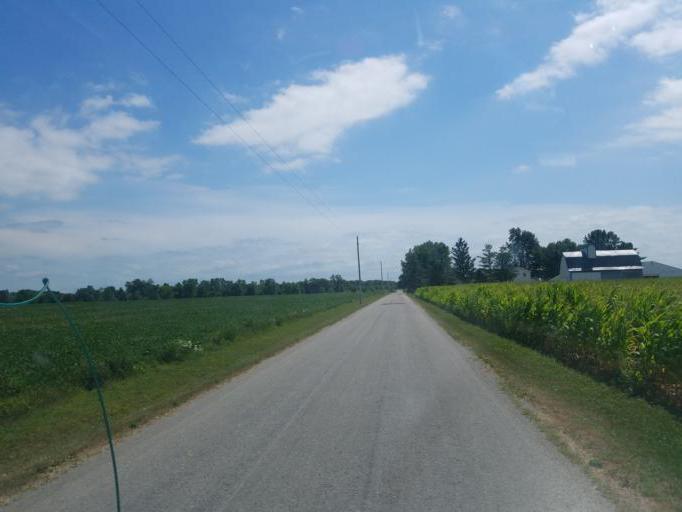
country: US
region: Indiana
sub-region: Allen County
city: Woodburn
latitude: 41.1736
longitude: -84.8694
